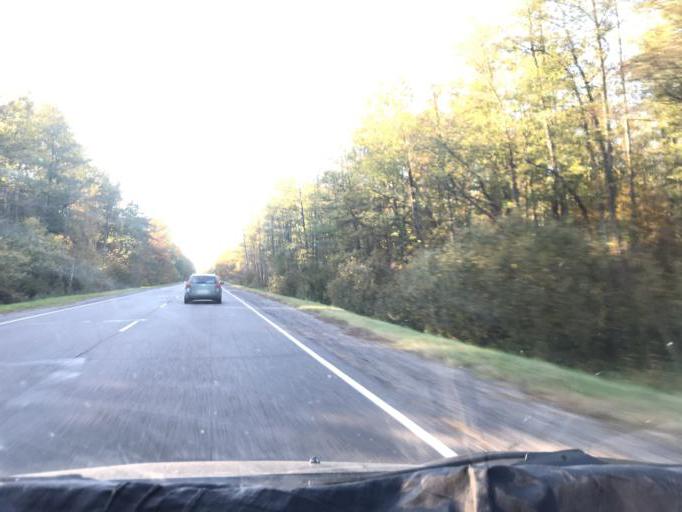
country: BY
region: Gomel
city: Pyetrykaw
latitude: 52.2692
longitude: 28.2853
